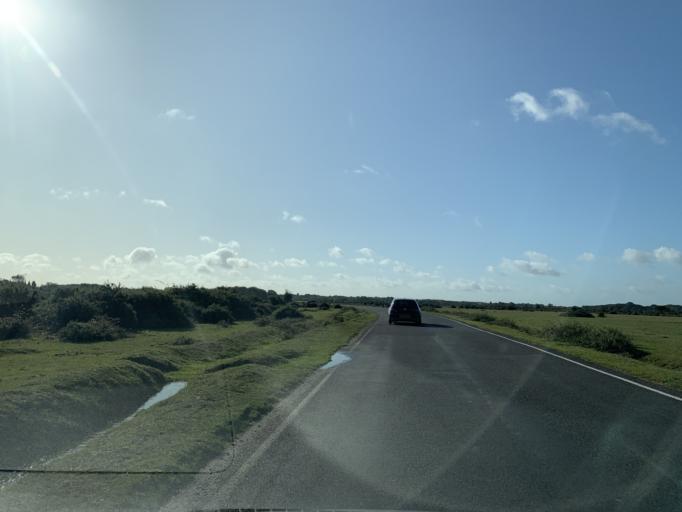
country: GB
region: England
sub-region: Hampshire
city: Cadnam
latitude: 50.9197
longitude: -1.6513
